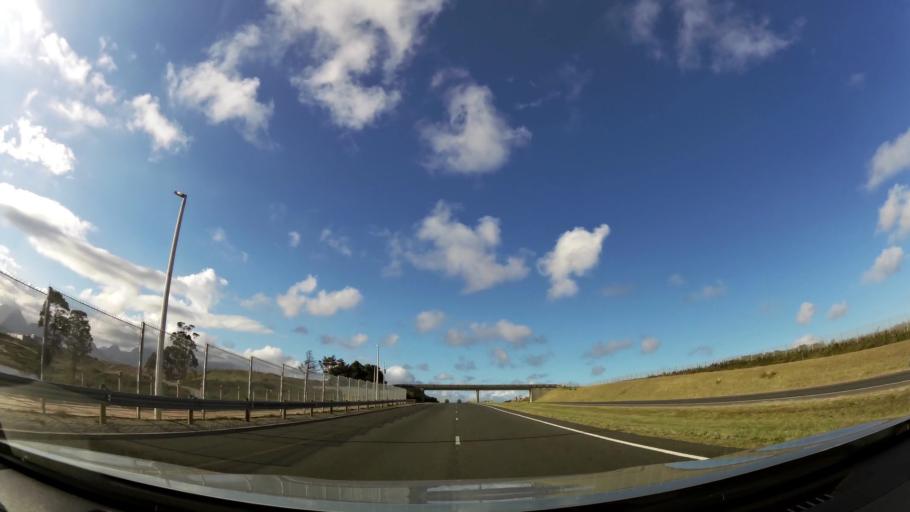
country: ZA
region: Western Cape
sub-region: Eden District Municipality
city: George
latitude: -33.9910
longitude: 22.4991
